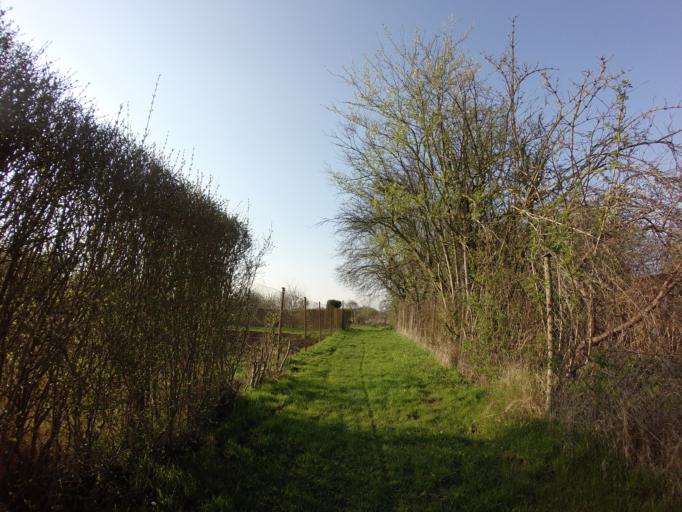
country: PL
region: West Pomeranian Voivodeship
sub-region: Powiat choszczenski
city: Choszczno
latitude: 53.1735
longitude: 15.4392
